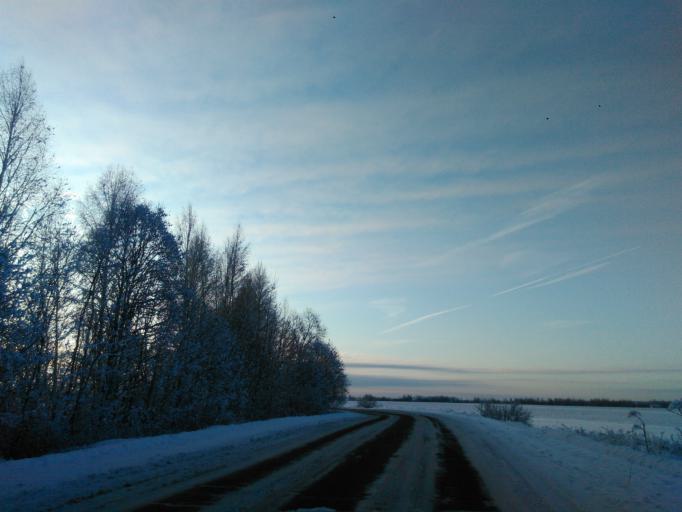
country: RU
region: Tverskaya
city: Zavidovo
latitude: 56.6220
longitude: 36.6150
